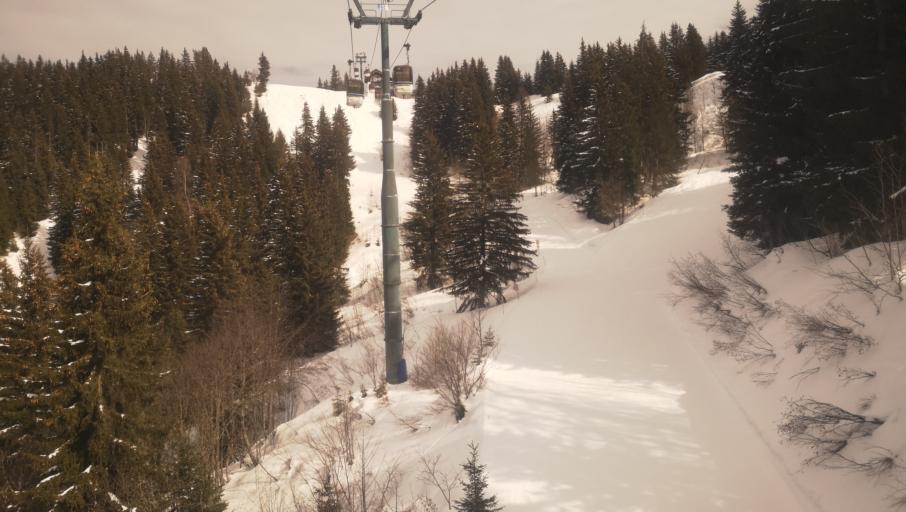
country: FR
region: Rhone-Alpes
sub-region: Departement de la Haute-Savoie
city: Megeve
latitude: 45.8568
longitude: 6.6515
